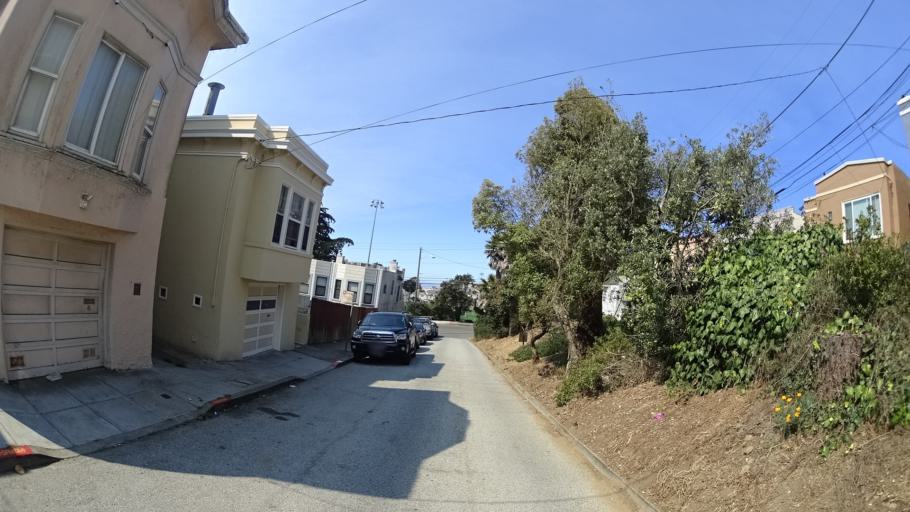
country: US
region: California
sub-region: San Mateo County
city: Daly City
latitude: 37.7158
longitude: -122.4555
